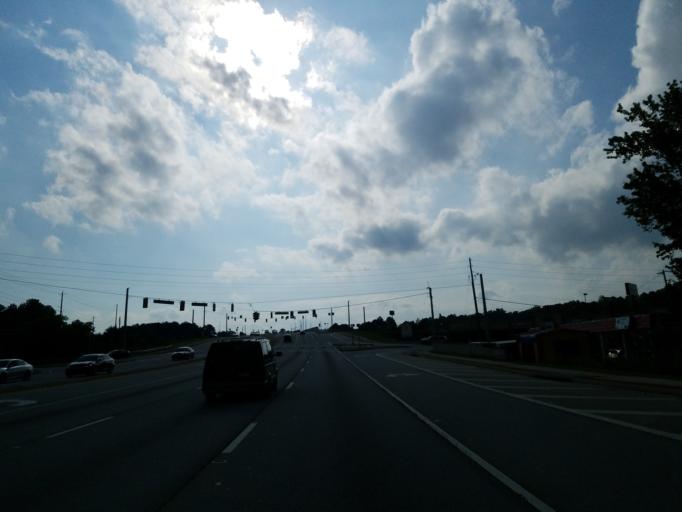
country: US
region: Georgia
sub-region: Douglas County
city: Douglasville
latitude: 33.7502
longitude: -84.7119
